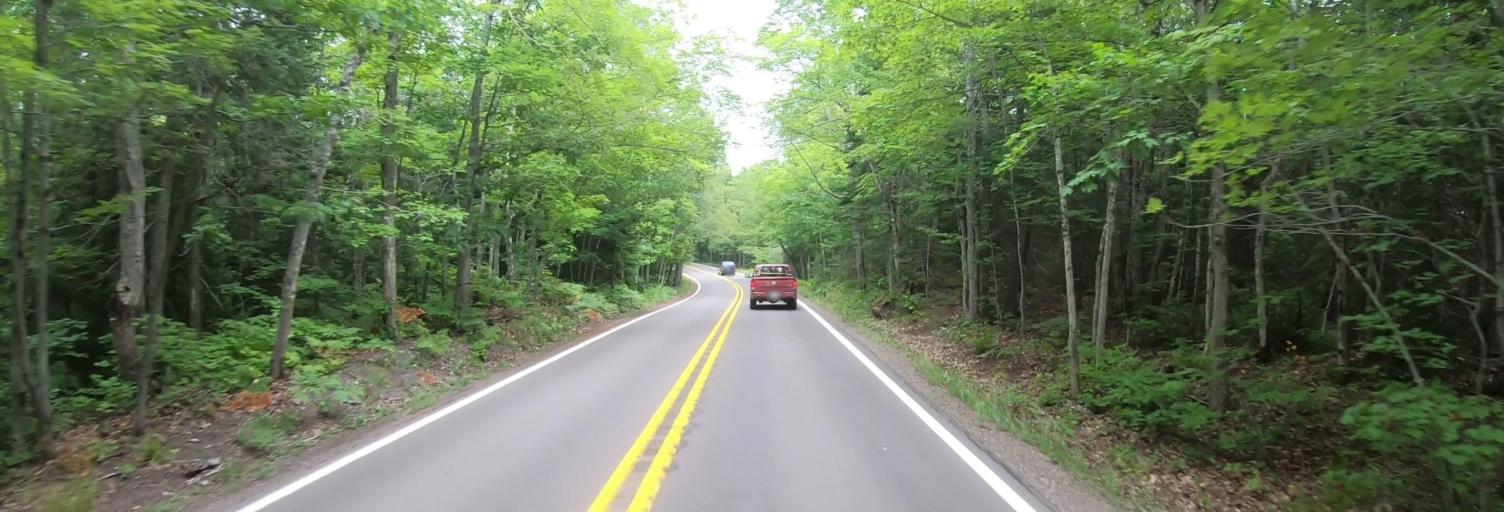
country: US
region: Michigan
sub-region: Keweenaw County
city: Eagle River
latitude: 47.4450
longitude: -87.9286
